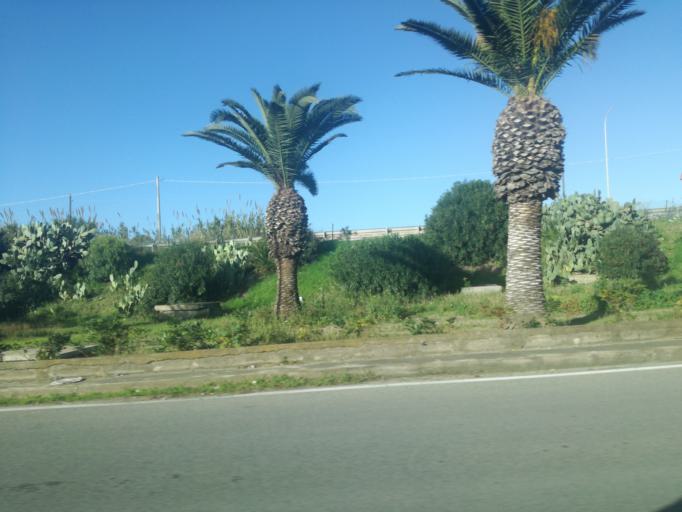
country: IT
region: Sicily
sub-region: Provincia di Caltanissetta
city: Gela
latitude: 37.0622
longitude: 14.2662
